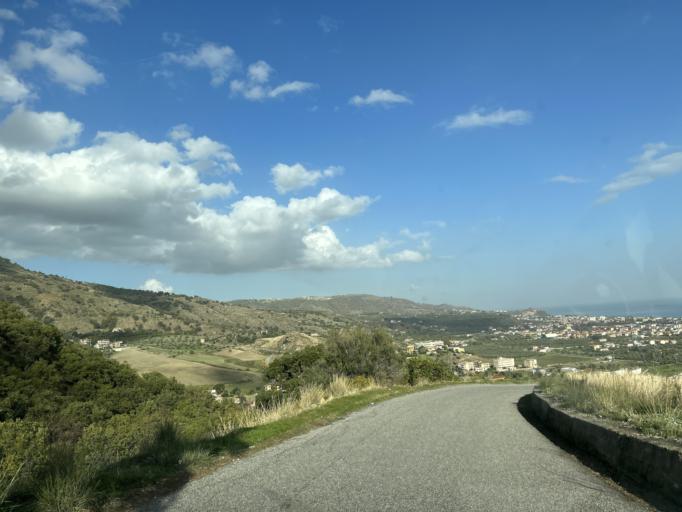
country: IT
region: Calabria
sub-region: Provincia di Catanzaro
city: Montepaone
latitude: 38.7173
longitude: 16.5144
